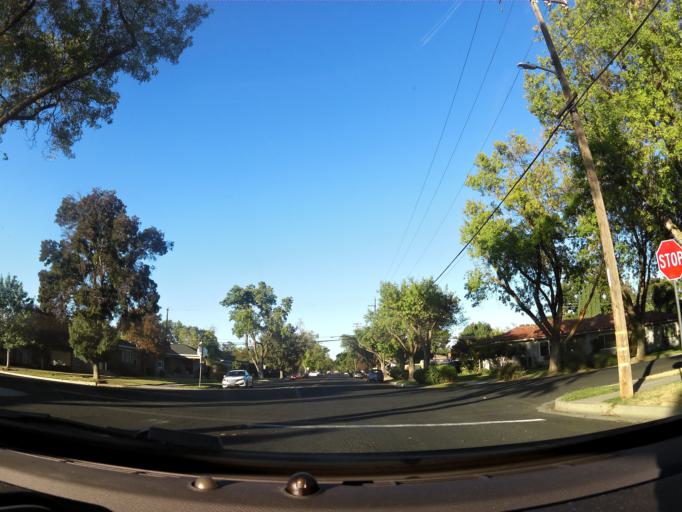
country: US
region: California
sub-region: Merced County
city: Merced
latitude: 37.3076
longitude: -120.4944
